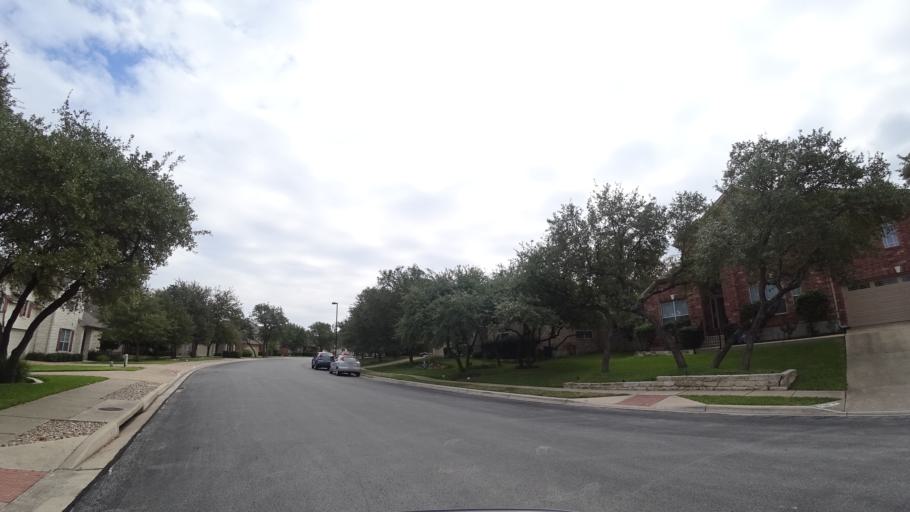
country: US
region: Texas
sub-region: Travis County
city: Shady Hollow
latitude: 30.1902
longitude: -97.9020
